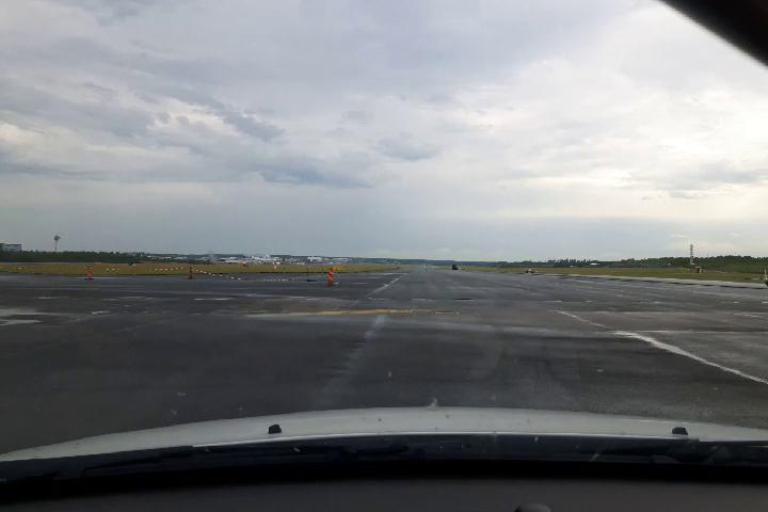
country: SE
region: Stockholm
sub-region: Sigtuna Kommun
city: Rosersberg
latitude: 59.6275
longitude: 17.9509
